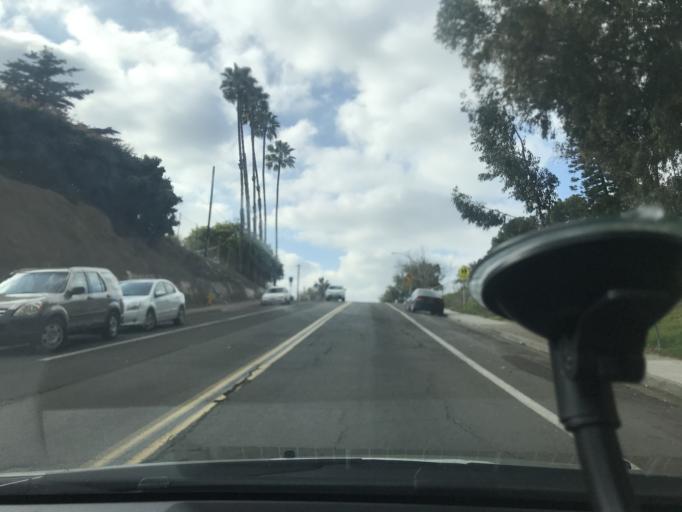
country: US
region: California
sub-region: San Diego County
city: San Diego
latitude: 32.8050
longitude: -117.1326
